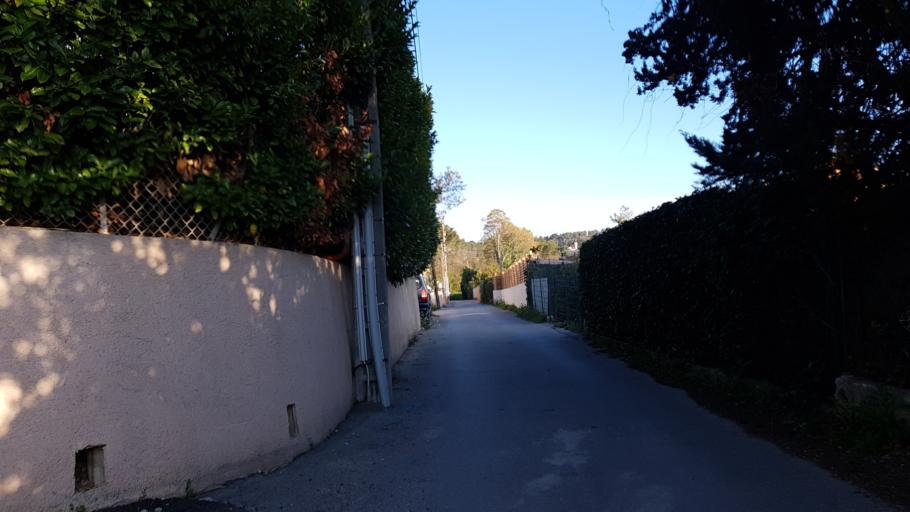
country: FR
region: Provence-Alpes-Cote d'Azur
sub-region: Departement des Bouches-du-Rhone
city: Bouc-Bel-Air
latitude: 43.4862
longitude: 5.4230
